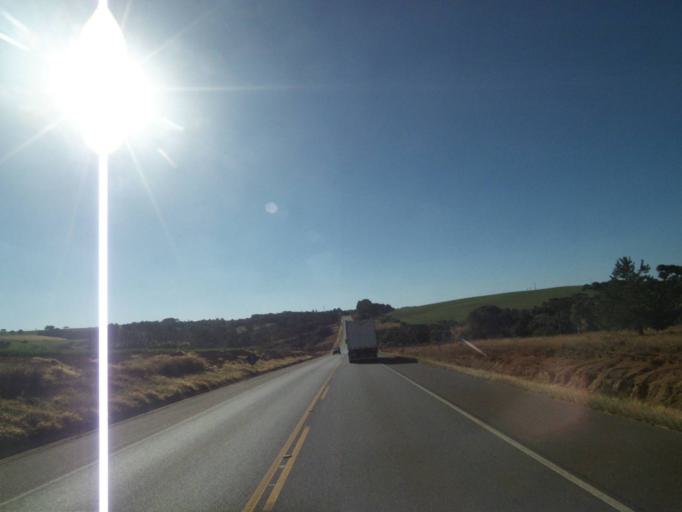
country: BR
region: Parana
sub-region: Tibagi
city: Tibagi
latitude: -24.5381
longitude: -50.4469
